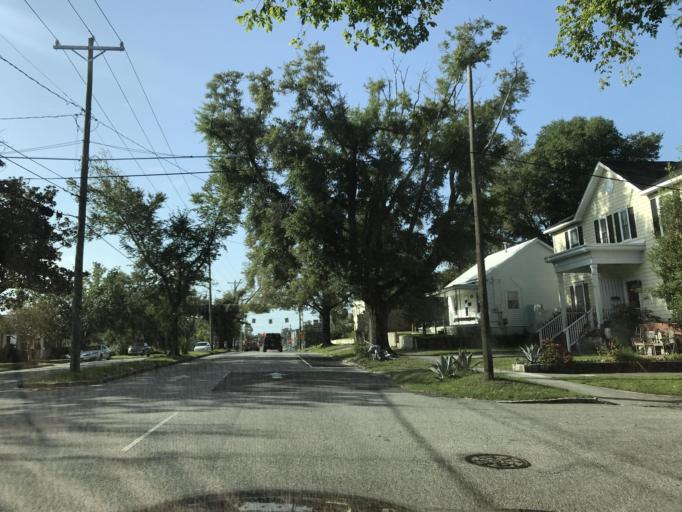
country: US
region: North Carolina
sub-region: New Hanover County
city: Wilmington
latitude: 34.2269
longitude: -77.9451
